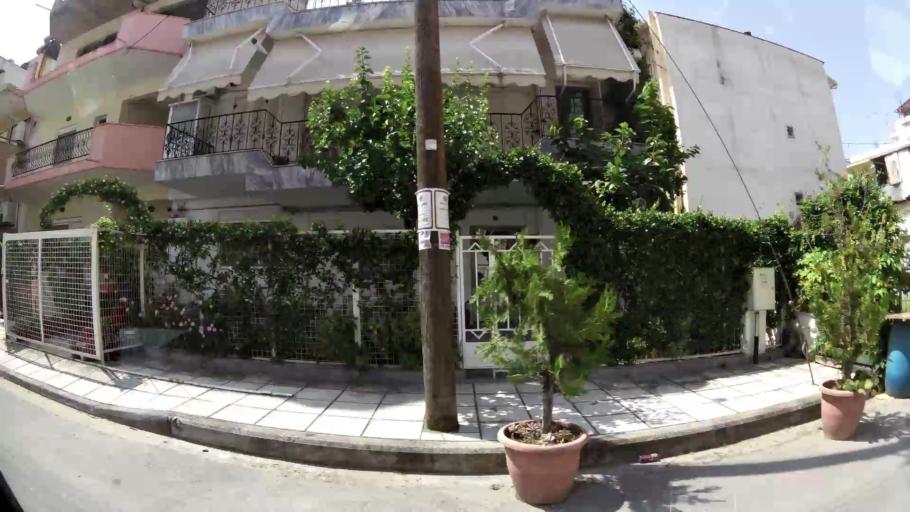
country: GR
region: Central Macedonia
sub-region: Nomos Thessalonikis
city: Evosmos
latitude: 40.6711
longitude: 22.9160
